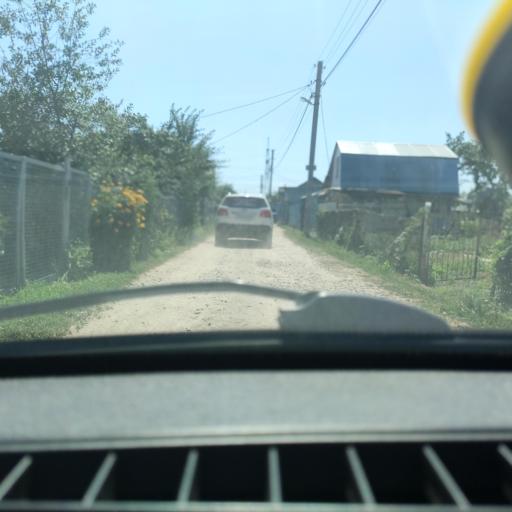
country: RU
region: Samara
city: Tol'yatti
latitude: 53.5920
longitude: 49.3047
